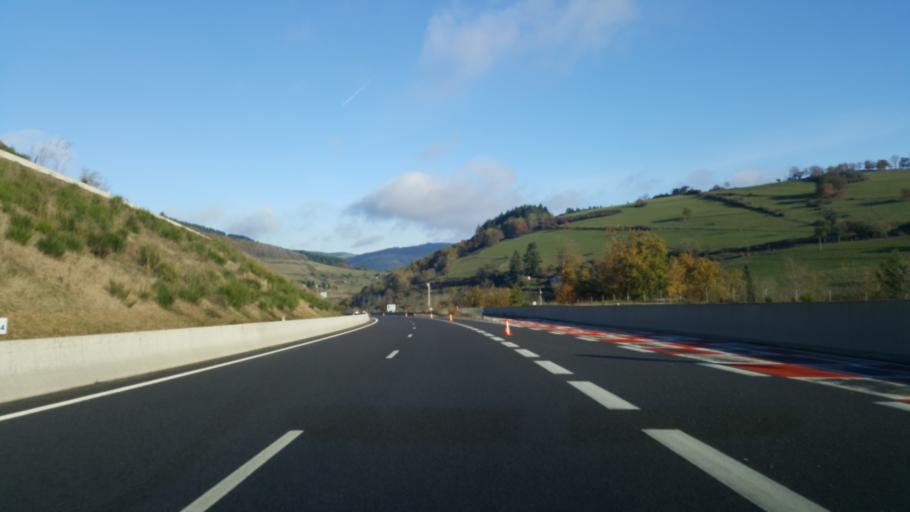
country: FR
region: Rhone-Alpes
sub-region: Departement du Rhone
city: Tarare
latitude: 45.8743
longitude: 4.3992
